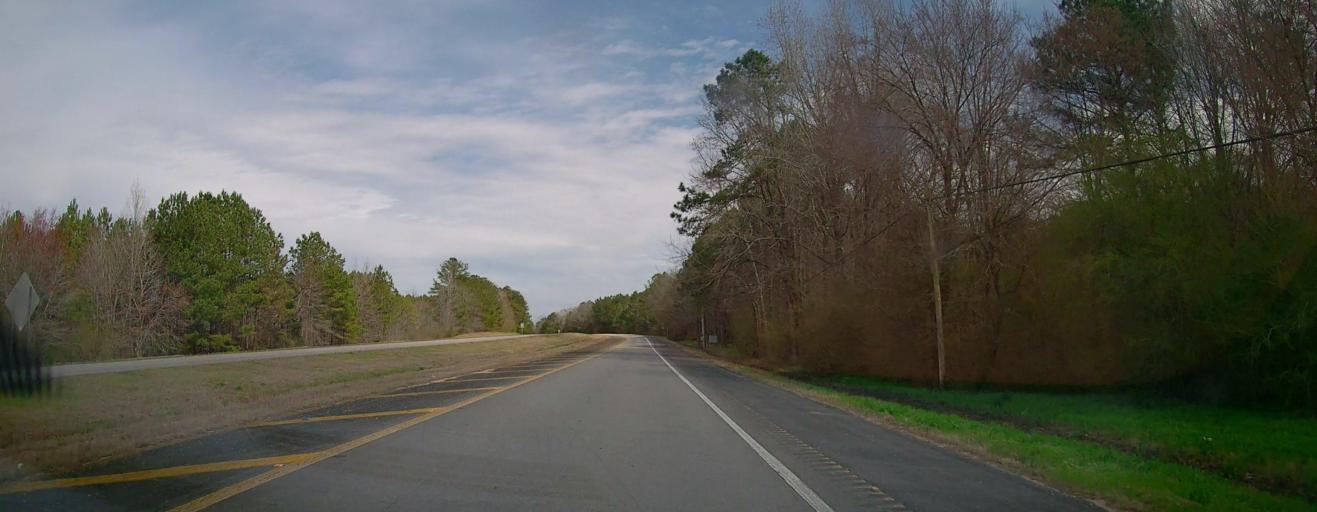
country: US
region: Alabama
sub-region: Marion County
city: Winfield
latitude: 33.9294
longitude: -87.6763
